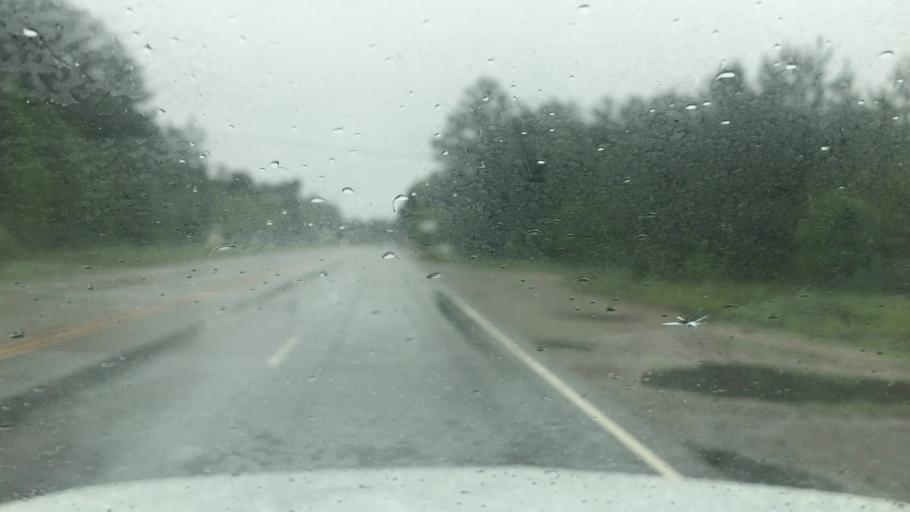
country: US
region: Virginia
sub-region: Hanover County
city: Ashland
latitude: 37.8147
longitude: -77.4738
